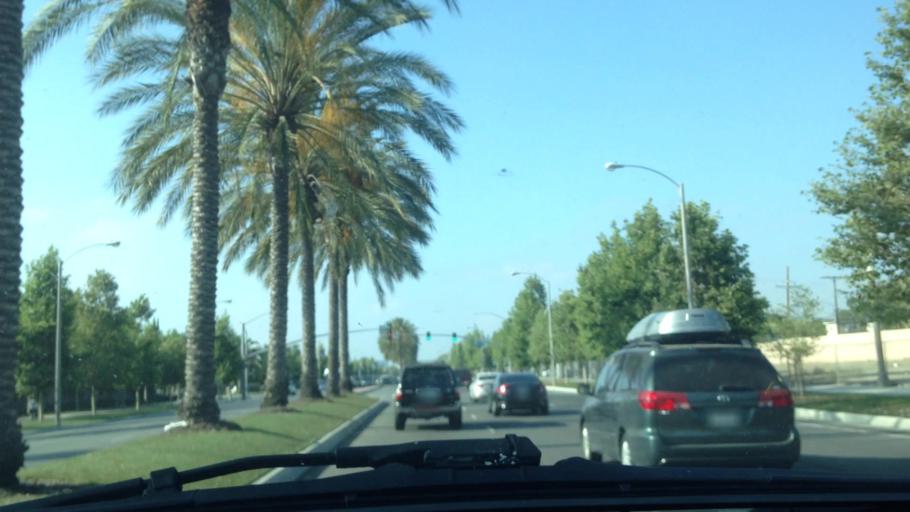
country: US
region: California
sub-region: Orange County
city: Santa Ana
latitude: 33.7412
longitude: -117.8853
